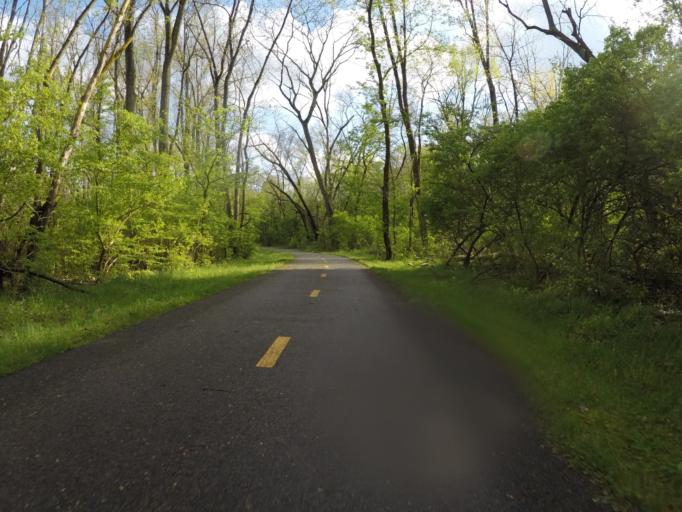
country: US
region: Ohio
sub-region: Franklin County
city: Bexley
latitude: 39.9995
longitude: -82.9372
